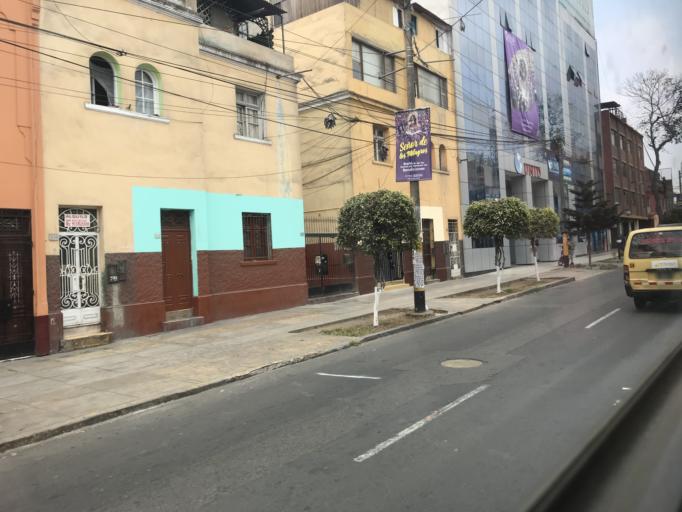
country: PE
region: Lima
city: Lima
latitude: -12.0565
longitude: -77.0449
